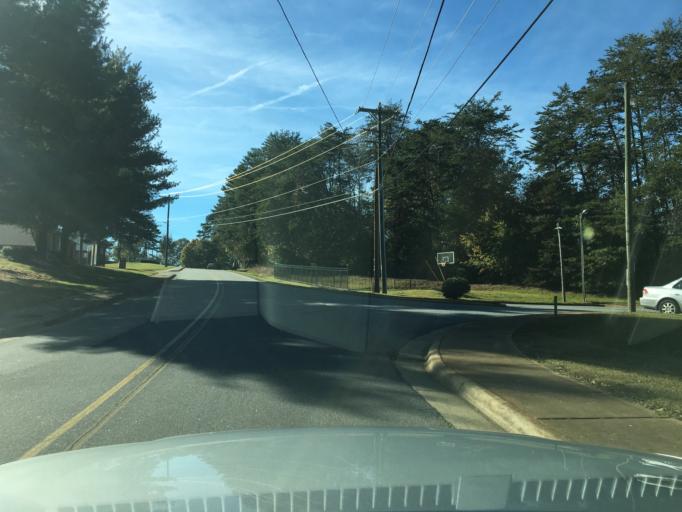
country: US
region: North Carolina
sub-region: Catawba County
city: Saint Stephens
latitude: 35.7094
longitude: -81.2742
